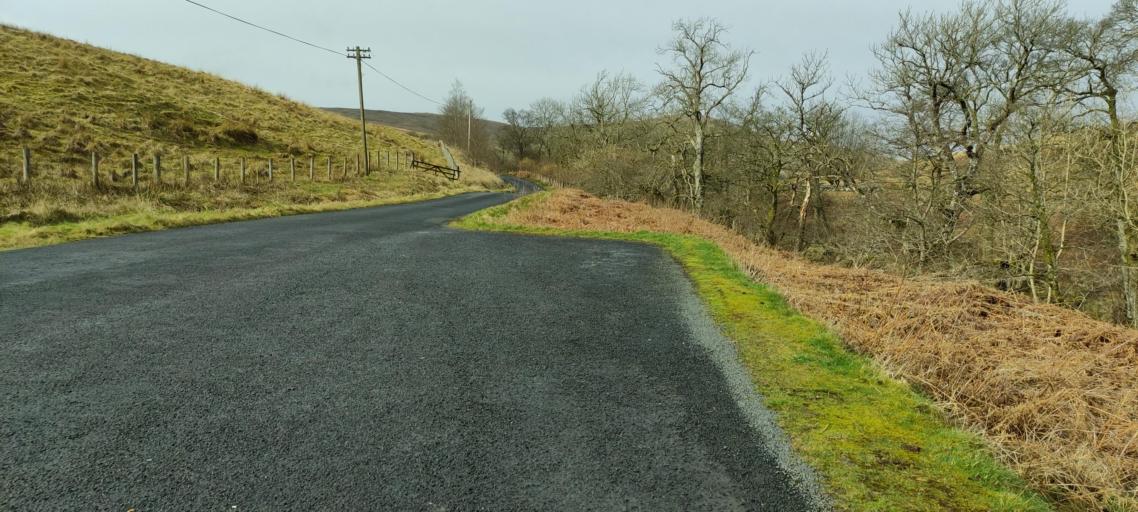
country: GB
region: Scotland
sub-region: The Scottish Borders
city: Hawick
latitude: 55.2553
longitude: -2.7960
